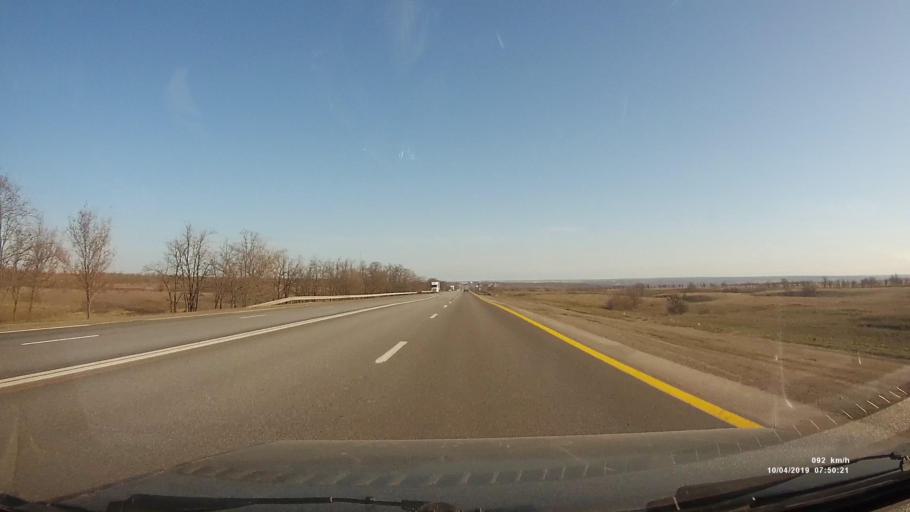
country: RU
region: Rostov
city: Kamensk-Shakhtinskiy
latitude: 48.2589
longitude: 40.2933
